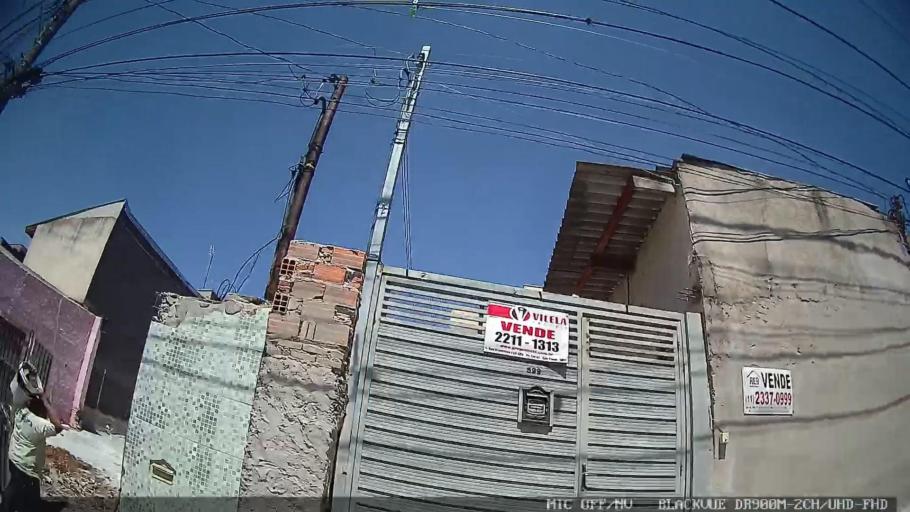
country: BR
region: Sao Paulo
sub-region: Sao Caetano Do Sul
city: Sao Caetano do Sul
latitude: -23.5925
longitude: -46.5344
